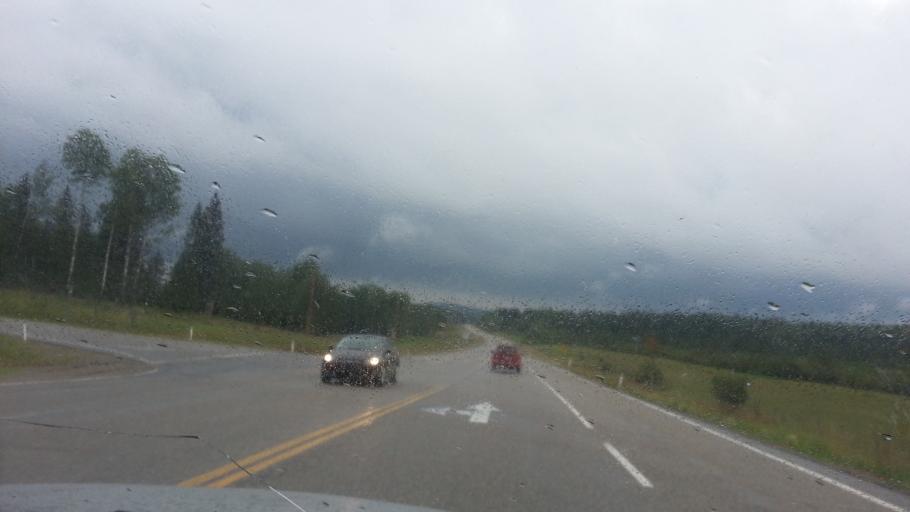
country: CA
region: Alberta
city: Cochrane
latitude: 50.9214
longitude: -114.5840
